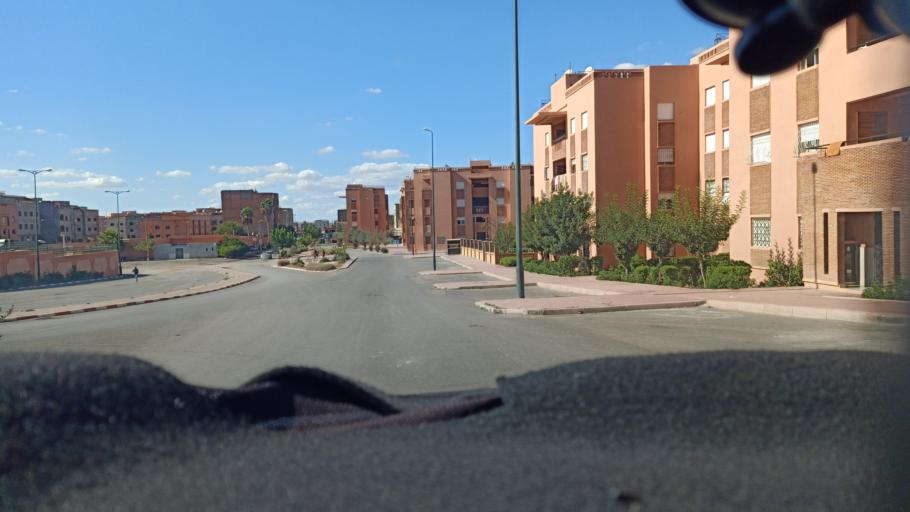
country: MA
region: Doukkala-Abda
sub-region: Safi
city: Youssoufia
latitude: 32.2400
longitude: -8.5338
